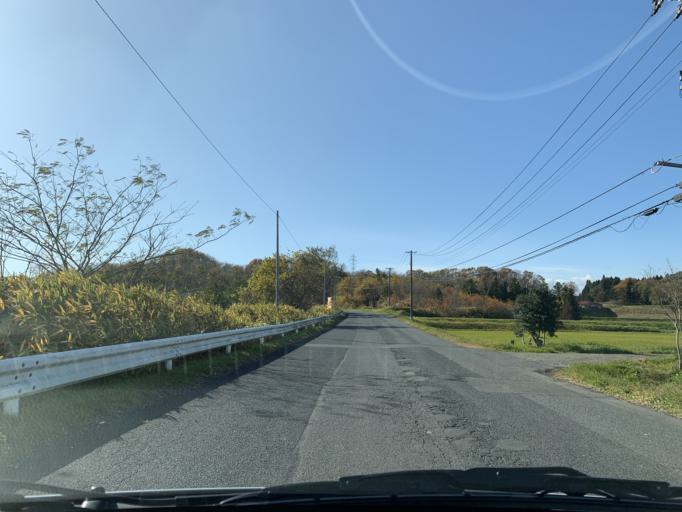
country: JP
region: Iwate
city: Mizusawa
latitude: 39.0320
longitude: 141.1128
